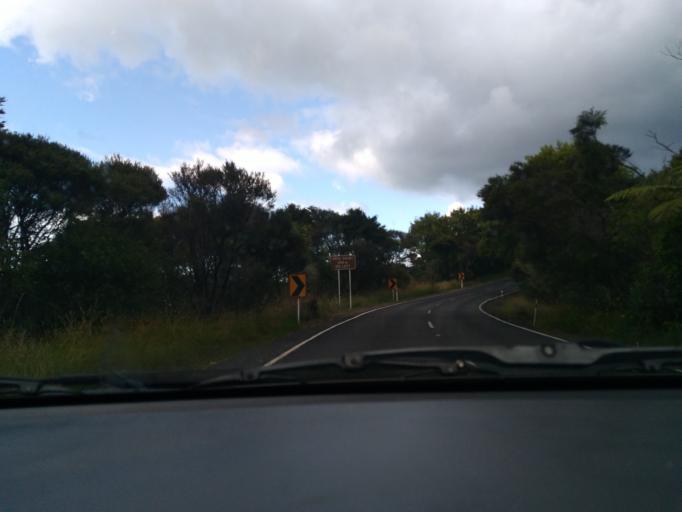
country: NZ
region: Auckland
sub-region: Auckland
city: Titirangi
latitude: -37.0067
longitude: 174.5815
